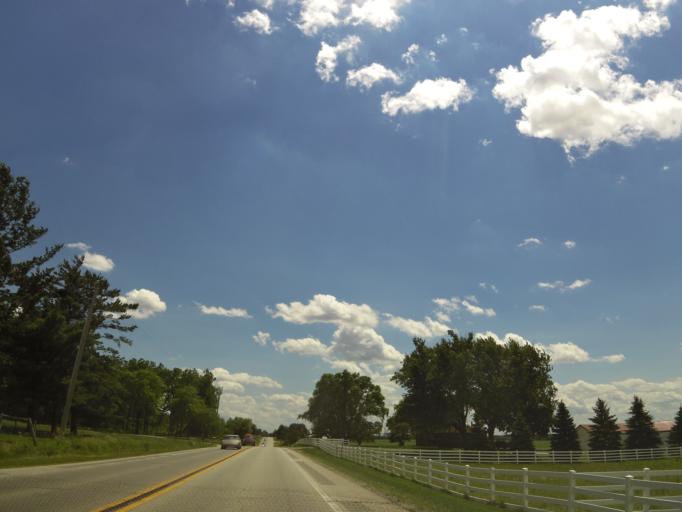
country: US
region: Iowa
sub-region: Buchanan County
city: Independence
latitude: 42.4950
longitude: -91.8895
